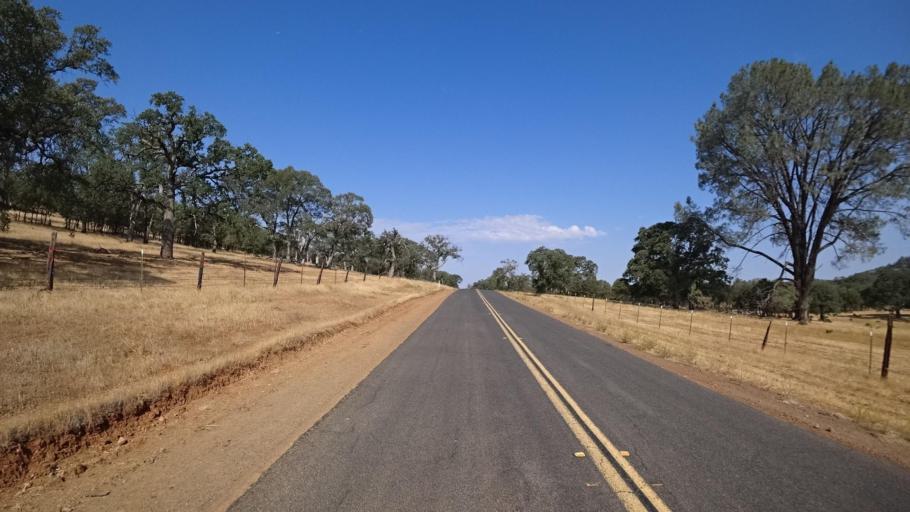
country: US
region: California
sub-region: Tuolumne County
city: Tuolumne City
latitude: 37.7198
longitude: -120.3026
